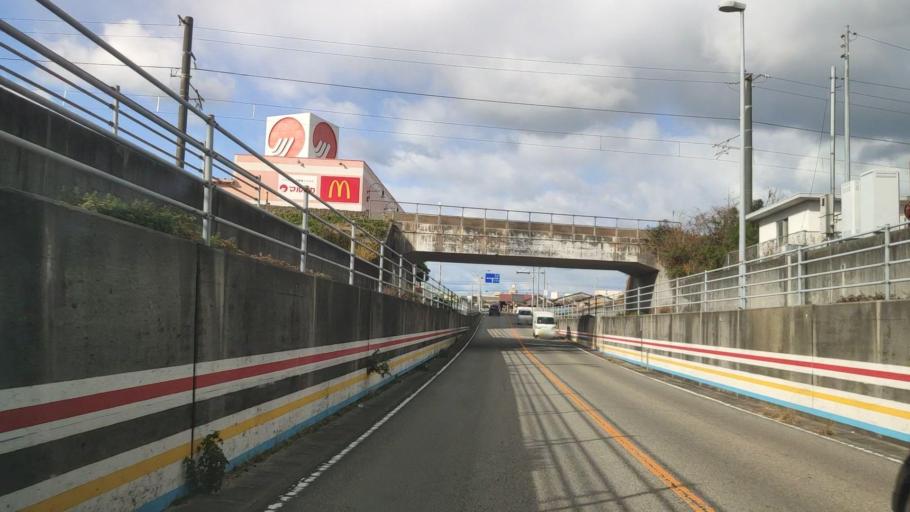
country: JP
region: Ehime
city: Hojo
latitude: 33.9817
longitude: 132.7799
